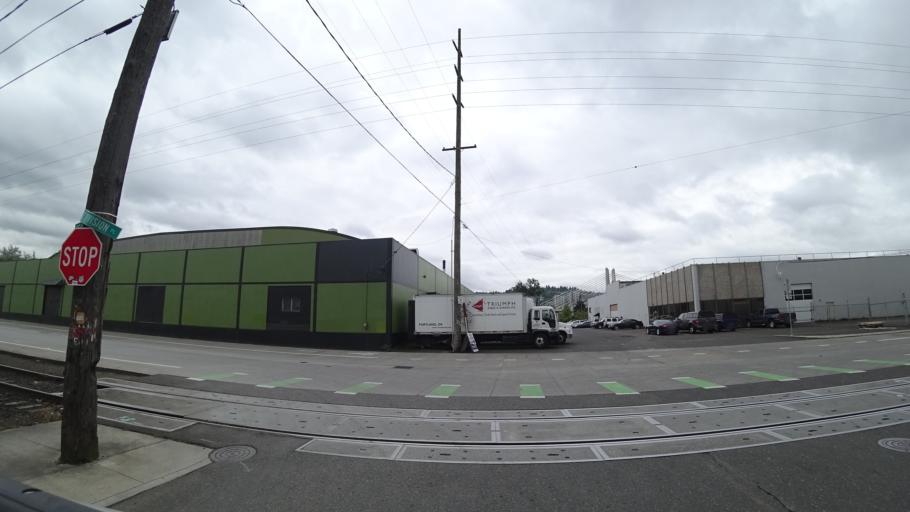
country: US
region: Oregon
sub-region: Multnomah County
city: Portland
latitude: 45.5049
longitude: -122.6617
